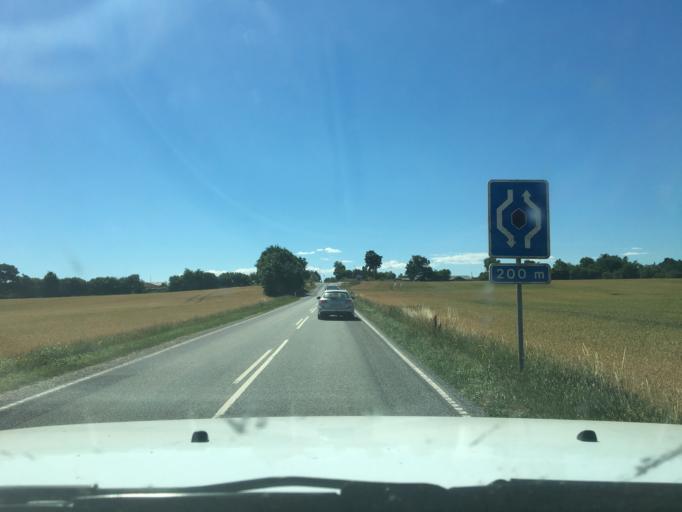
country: DK
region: Central Jutland
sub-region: Syddjurs Kommune
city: Hornslet
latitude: 56.3248
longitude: 10.3267
